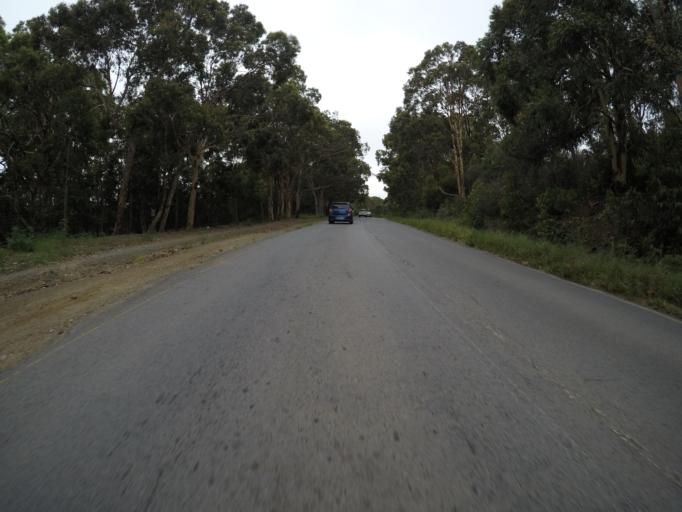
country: ZA
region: Eastern Cape
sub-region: Buffalo City Metropolitan Municipality
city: East London
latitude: -32.9373
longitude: 27.9435
